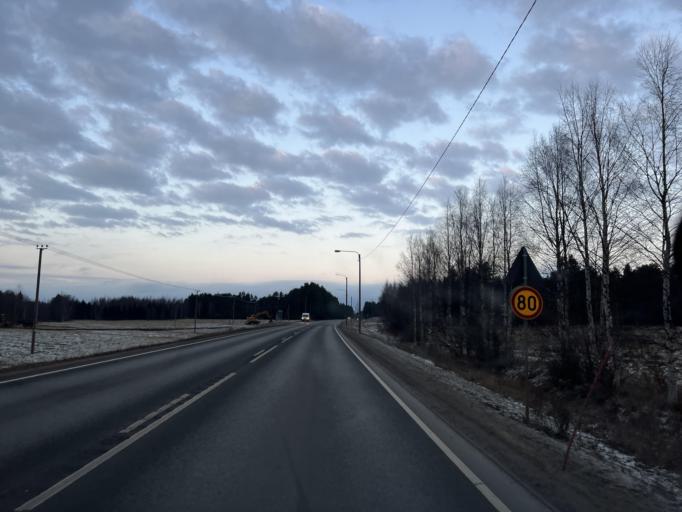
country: FI
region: Northern Ostrobothnia
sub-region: Oulu
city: Muhos
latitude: 64.8719
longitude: 25.8628
